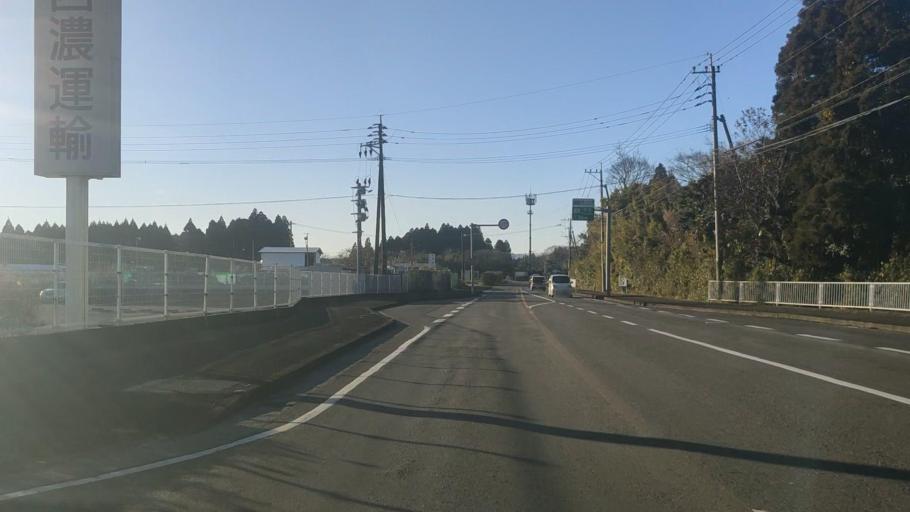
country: JP
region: Miyazaki
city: Miyazaki-shi
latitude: 31.8578
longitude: 131.3791
